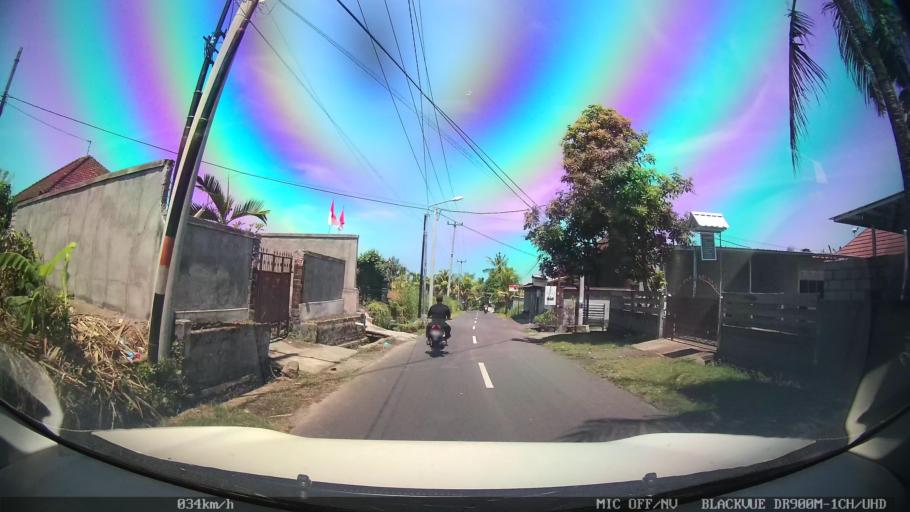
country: ID
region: Bali
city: Banjar Pasekan
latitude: -8.5649
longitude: 115.3200
